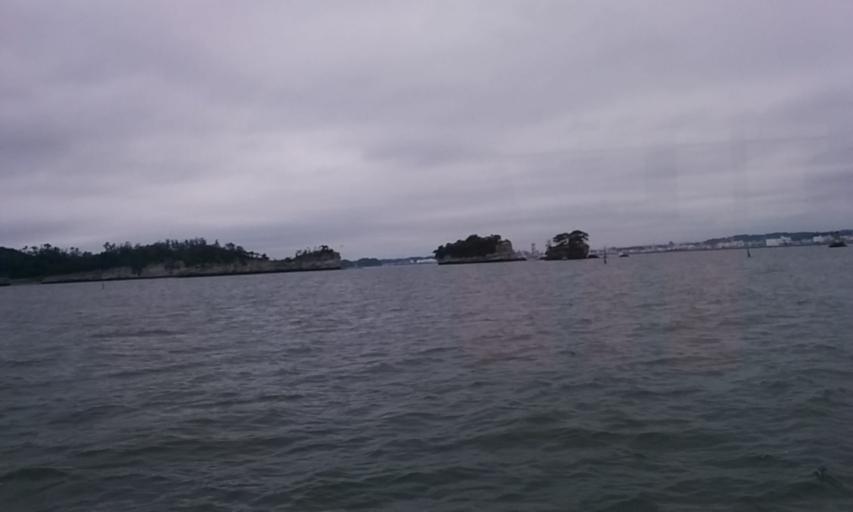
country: JP
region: Miyagi
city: Matsushima
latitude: 38.3324
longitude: 141.0741
